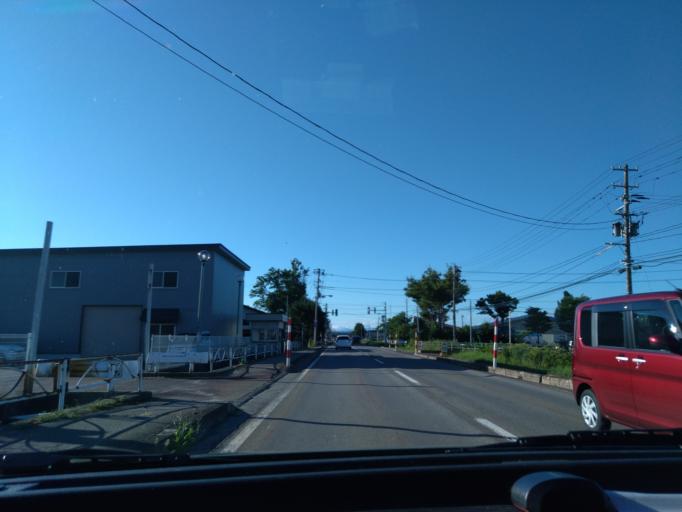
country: JP
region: Akita
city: Omagari
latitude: 39.4308
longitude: 140.4858
